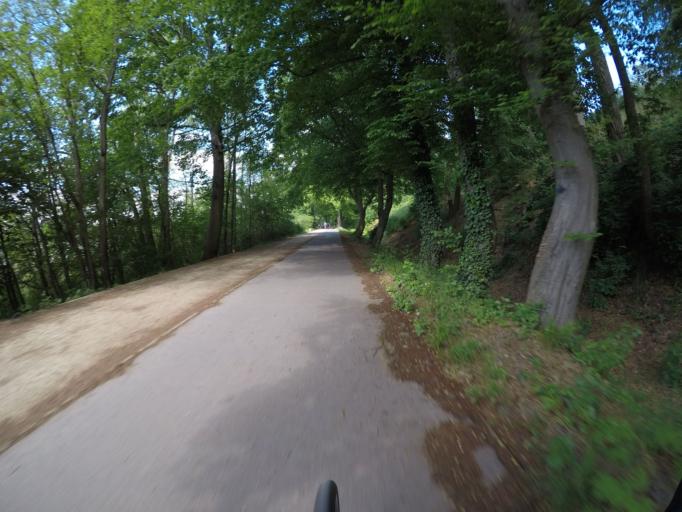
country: DE
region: Brandenburg
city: Potsdam
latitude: 52.4205
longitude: 13.0984
